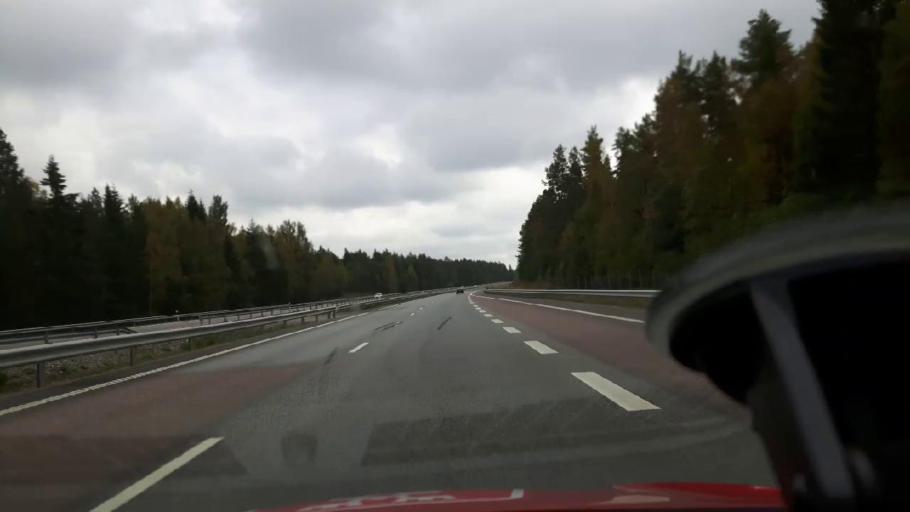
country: SE
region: Gaevleborg
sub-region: Gavle Kommun
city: Gavle
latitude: 60.6359
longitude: 17.1442
